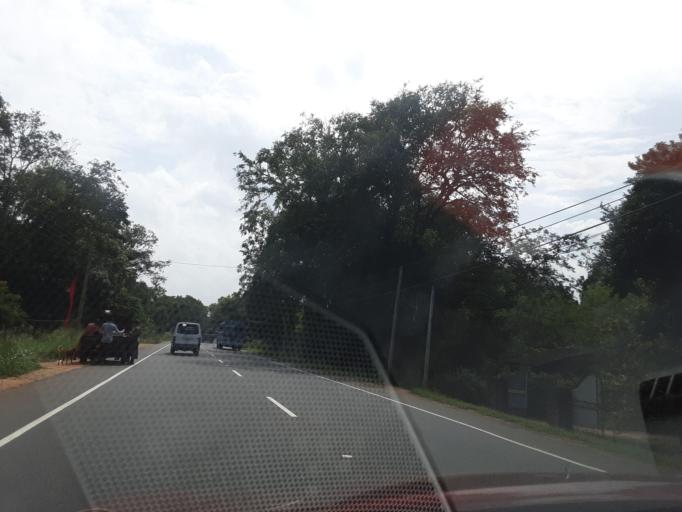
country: LK
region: North Central
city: Anuradhapura
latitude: 8.4936
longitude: 80.5120
